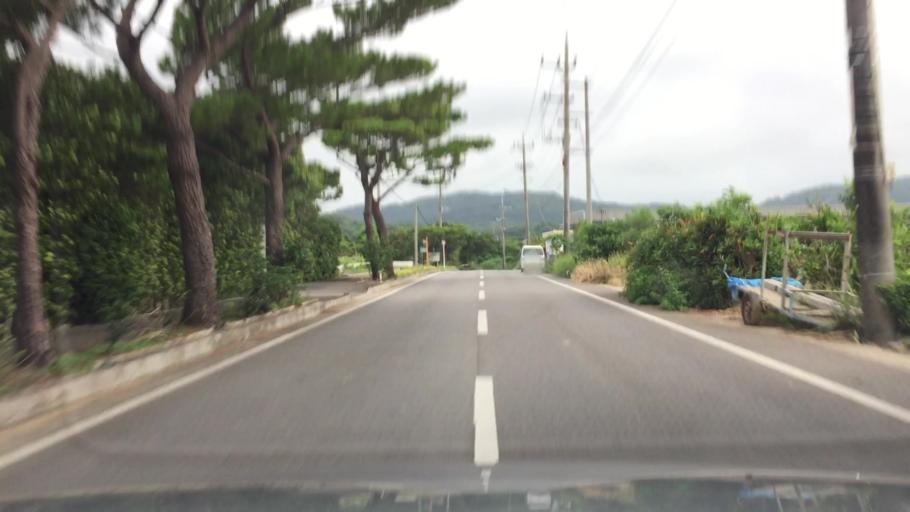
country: JP
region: Okinawa
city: Ishigaki
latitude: 24.3915
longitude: 124.1553
